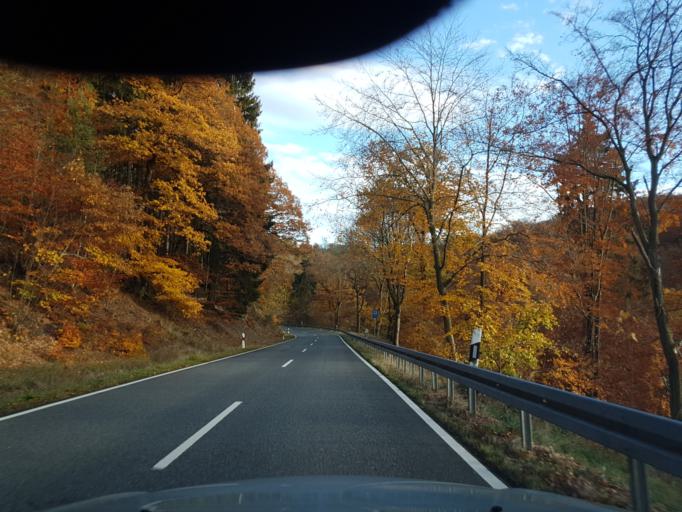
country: DE
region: Hesse
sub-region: Regierungsbezirk Darmstadt
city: Bad Schwalbach
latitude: 50.1292
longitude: 8.0402
